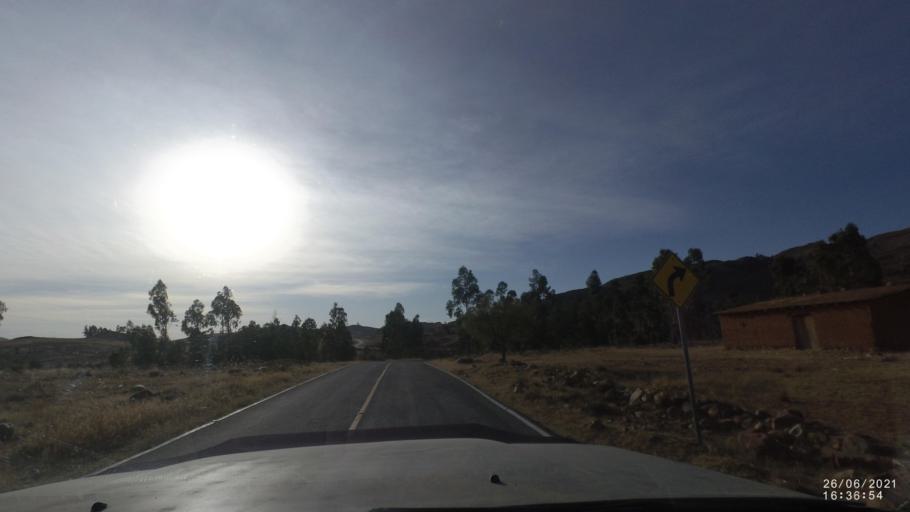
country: BO
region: Cochabamba
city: Arani
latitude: -17.7861
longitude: -65.8092
